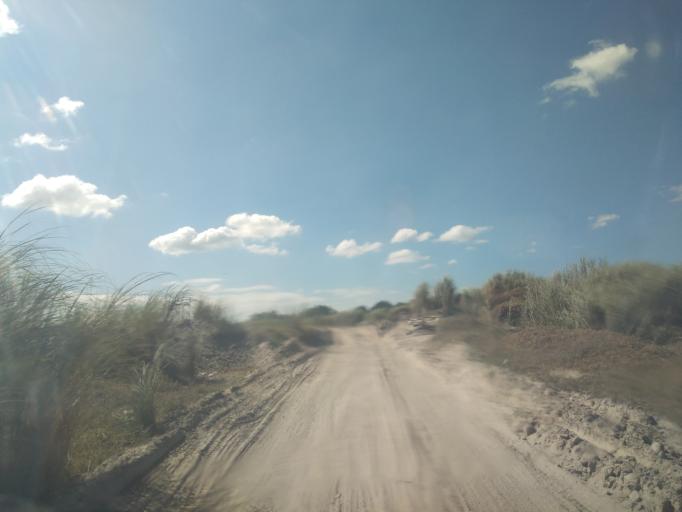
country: PH
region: Central Luzon
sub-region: Province of Pampanga
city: Balas
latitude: 15.0788
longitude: 120.6028
